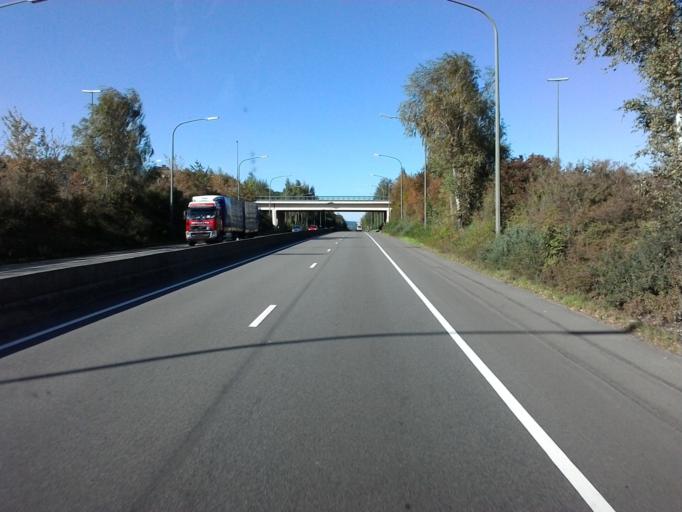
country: BE
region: Wallonia
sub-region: Province du Luxembourg
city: Messancy
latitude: 49.5861
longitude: 5.8089
